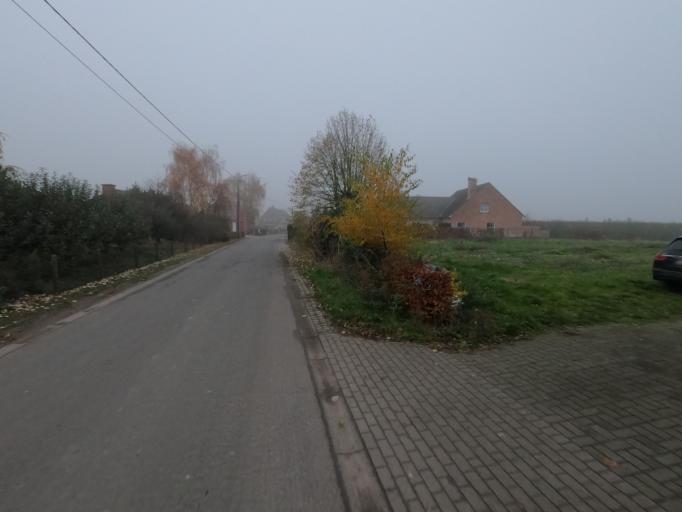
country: BE
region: Flanders
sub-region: Provincie Oost-Vlaanderen
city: Kruibeke
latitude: 51.1862
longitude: 4.3014
